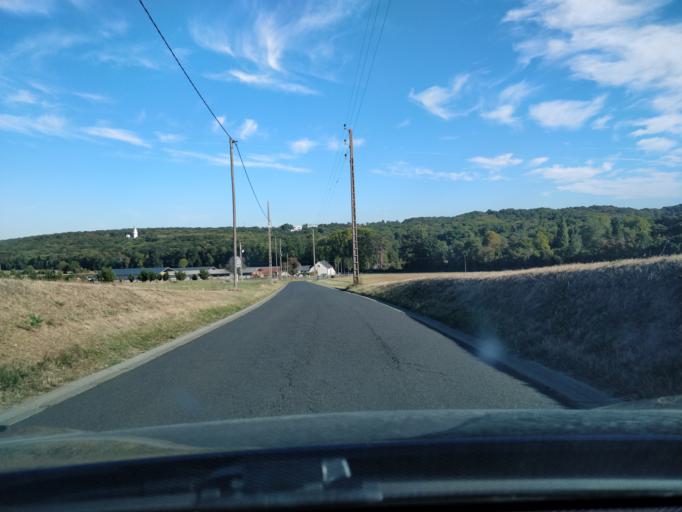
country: FR
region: Ile-de-France
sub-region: Departement de l'Essonne
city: Forges-les-Bains
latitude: 48.6365
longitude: 2.0998
